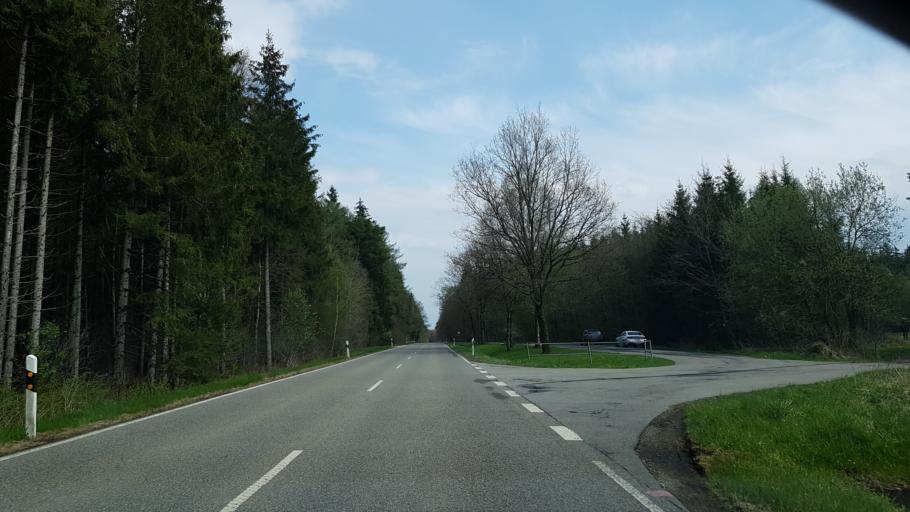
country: DE
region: Baden-Wuerttemberg
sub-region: Tuebingen Region
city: Wain
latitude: 48.2151
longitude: 9.9917
